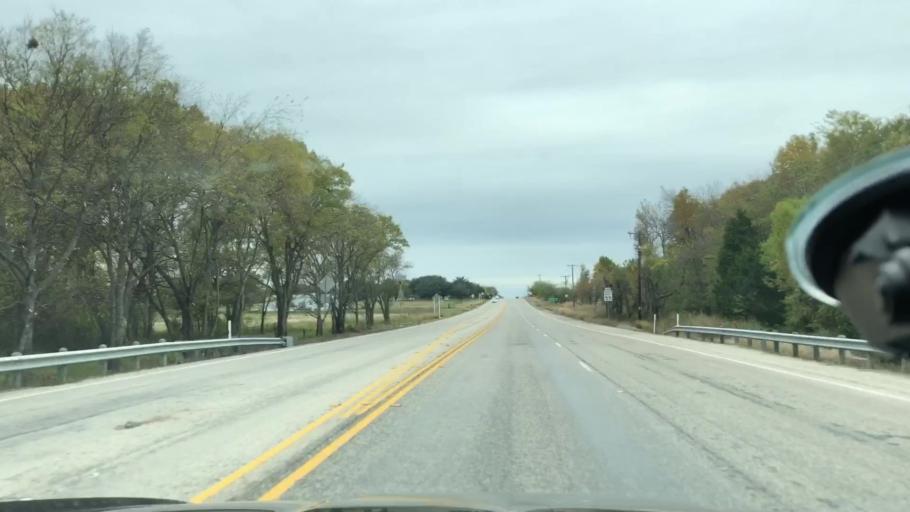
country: US
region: Texas
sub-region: Hunt County
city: Quinlan
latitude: 32.9482
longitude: -96.1074
